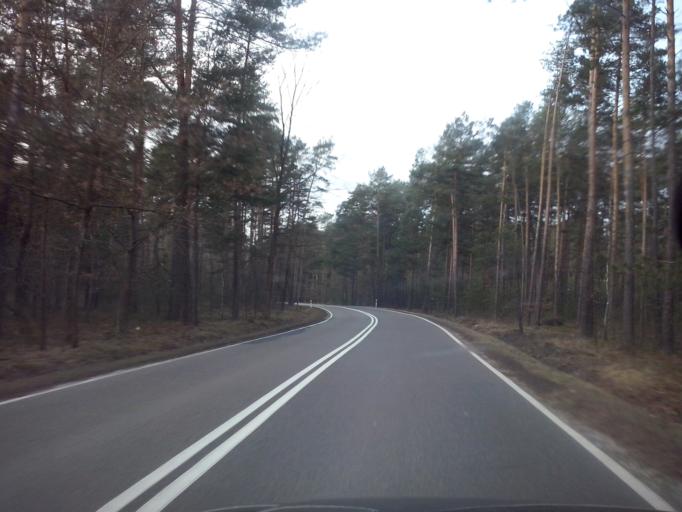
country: PL
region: Lublin Voivodeship
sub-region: Powiat bilgorajski
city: Biszcza
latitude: 50.5025
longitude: 22.6001
